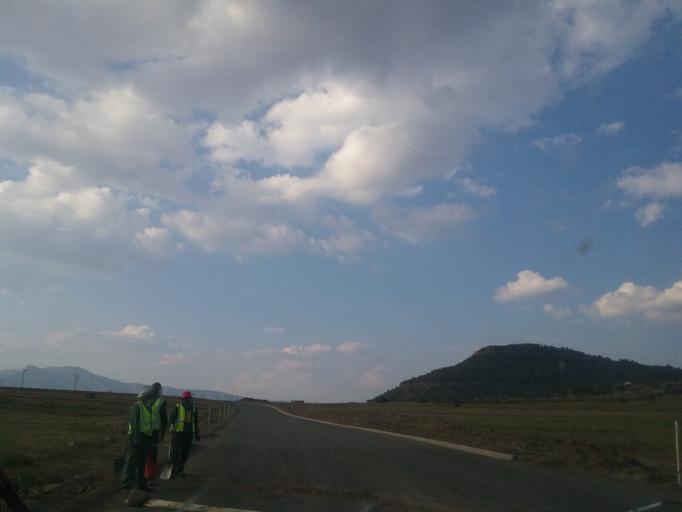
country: LS
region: Quthing
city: Quthing
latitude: -30.4060
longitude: 27.6074
